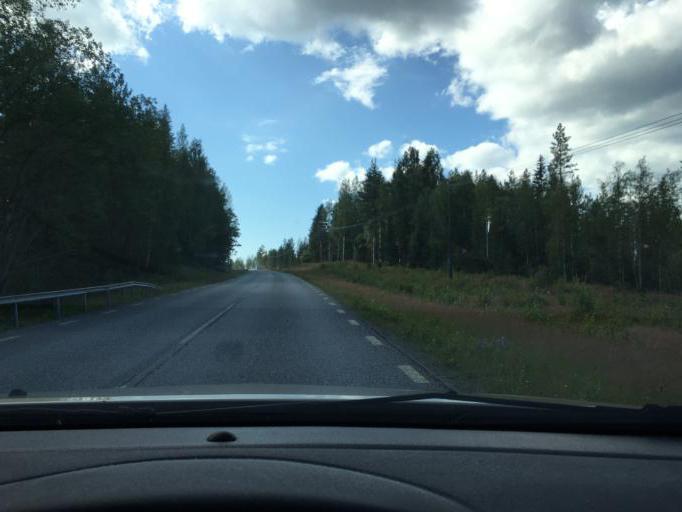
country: SE
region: Norrbotten
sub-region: Kalix Kommun
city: Toere
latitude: 66.0535
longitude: 22.5274
